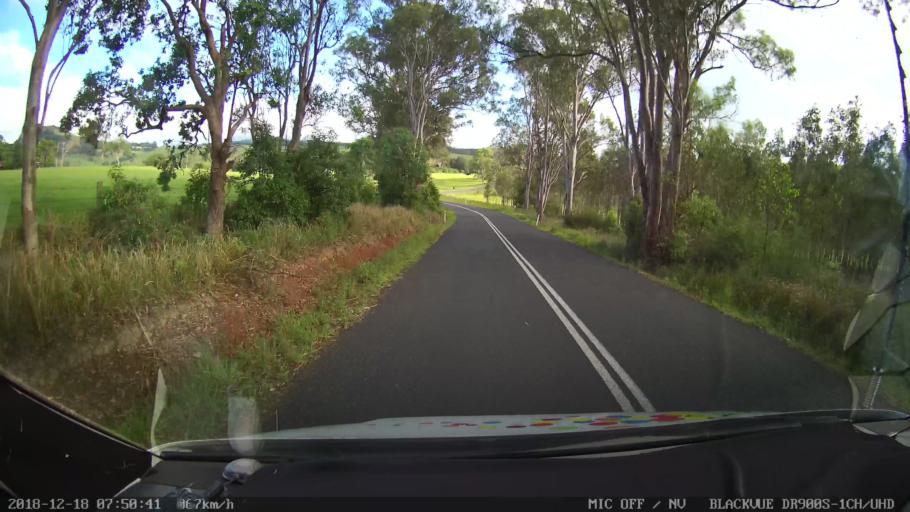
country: AU
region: New South Wales
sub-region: Kyogle
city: Kyogle
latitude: -28.4435
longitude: 152.5745
